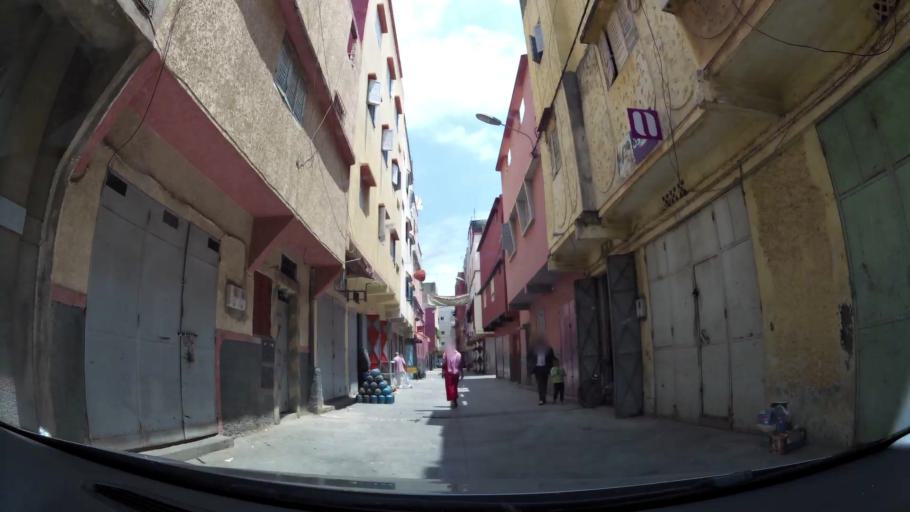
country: MA
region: Rabat-Sale-Zemmour-Zaer
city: Sale
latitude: 34.0523
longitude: -6.7899
